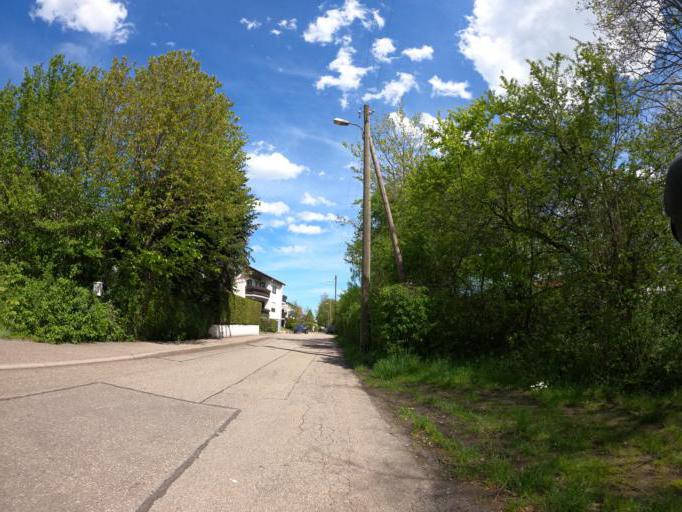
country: DE
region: Baden-Wuerttemberg
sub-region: Karlsruhe Region
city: Birkenfeld
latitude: 48.8842
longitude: 8.6537
